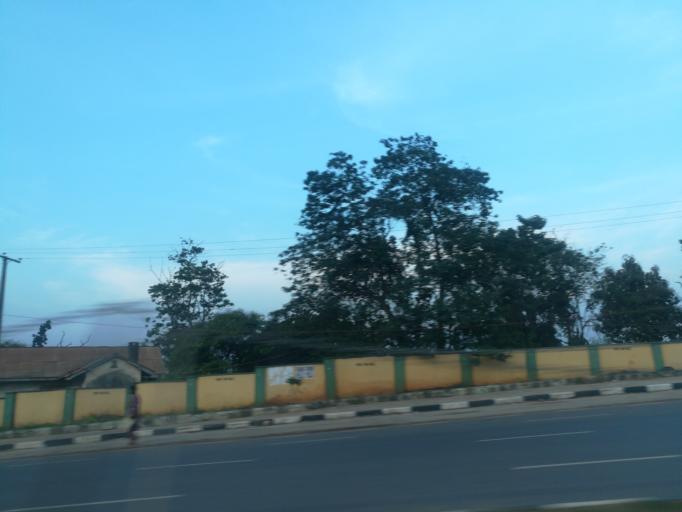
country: NG
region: Ogun
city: Abeokuta
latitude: 7.1700
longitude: 3.3714
